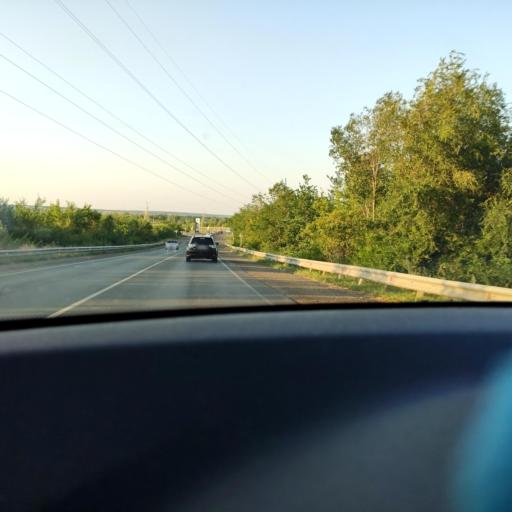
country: RU
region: Samara
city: Kinel'
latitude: 53.2440
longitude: 50.5838
